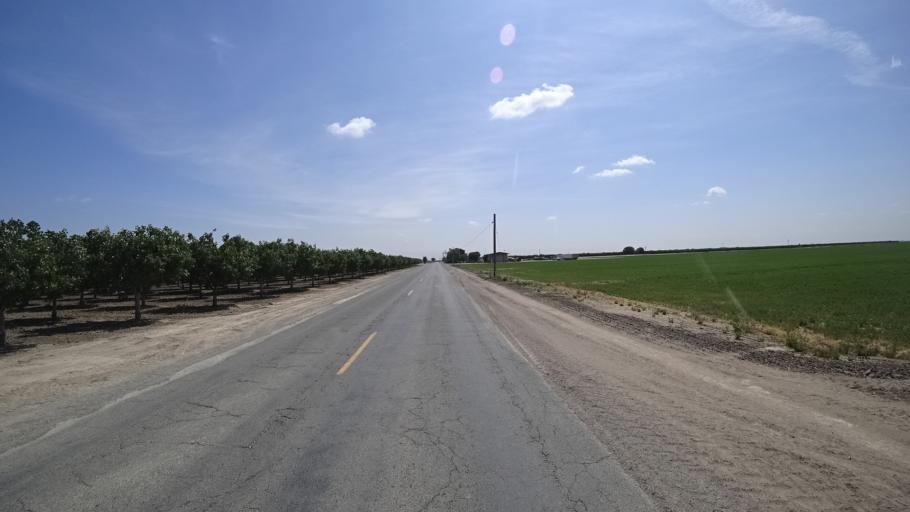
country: US
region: California
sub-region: Kings County
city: Home Garden
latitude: 36.2696
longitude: -119.5429
